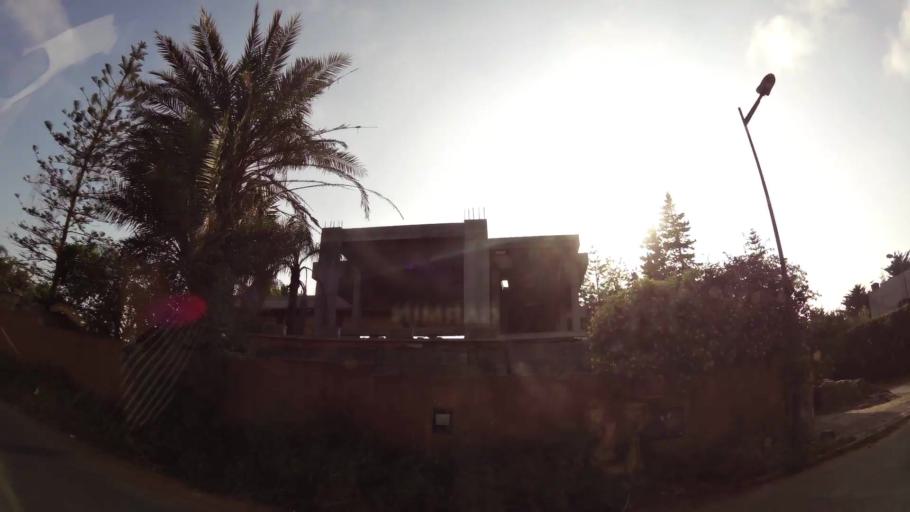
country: MA
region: Rabat-Sale-Zemmour-Zaer
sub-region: Rabat
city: Rabat
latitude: 33.9425
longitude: -6.8122
